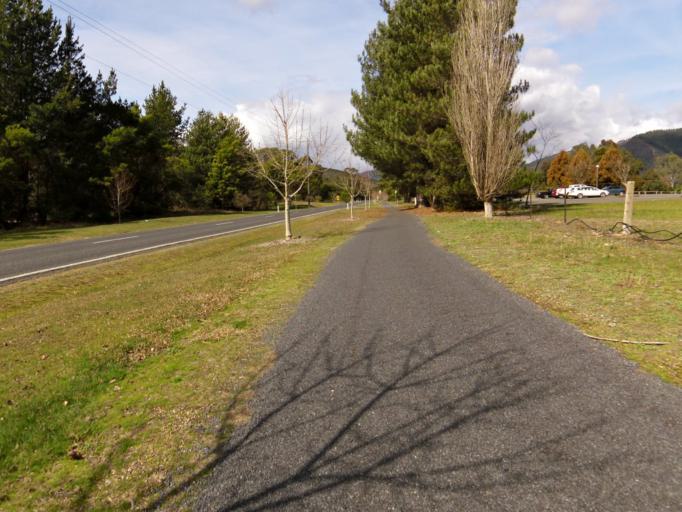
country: AU
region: Victoria
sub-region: Alpine
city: Mount Beauty
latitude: -36.7091
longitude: 146.9326
